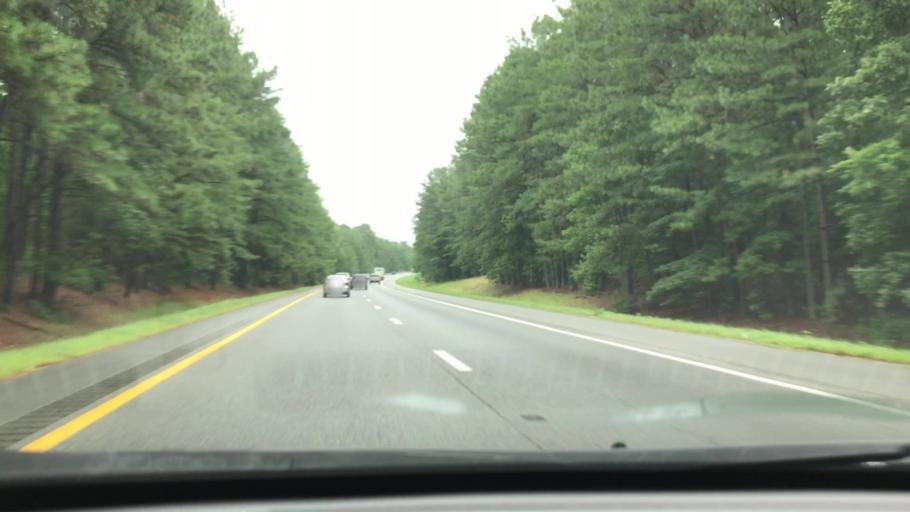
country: US
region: Virginia
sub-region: City of Emporia
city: Emporia
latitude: 36.7490
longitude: -77.5120
